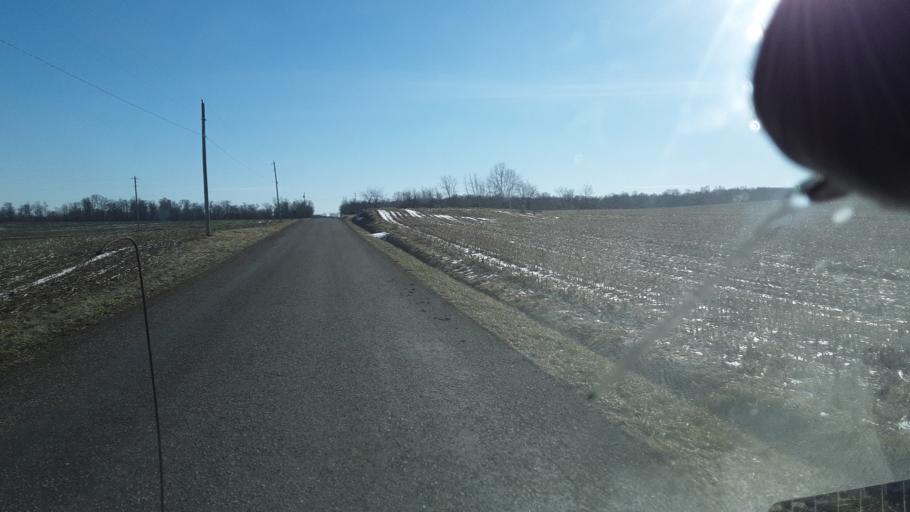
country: US
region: Ohio
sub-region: Ashland County
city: Loudonville
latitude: 40.7393
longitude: -82.2215
